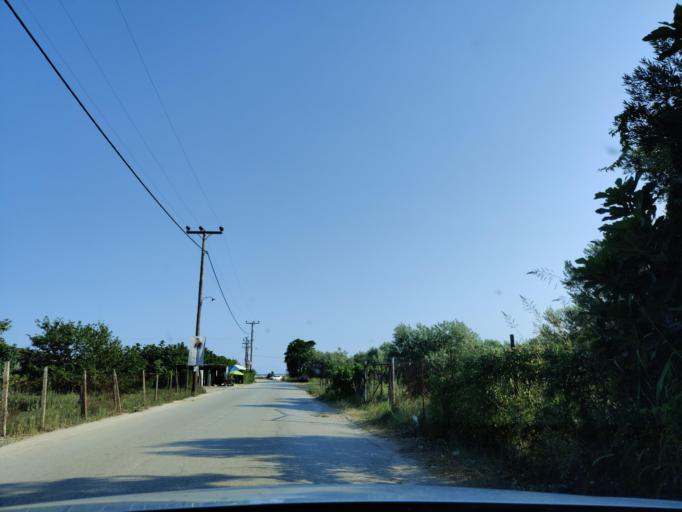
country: GR
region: East Macedonia and Thrace
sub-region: Nomos Kavalas
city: Nea Peramos
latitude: 40.8214
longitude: 24.3078
